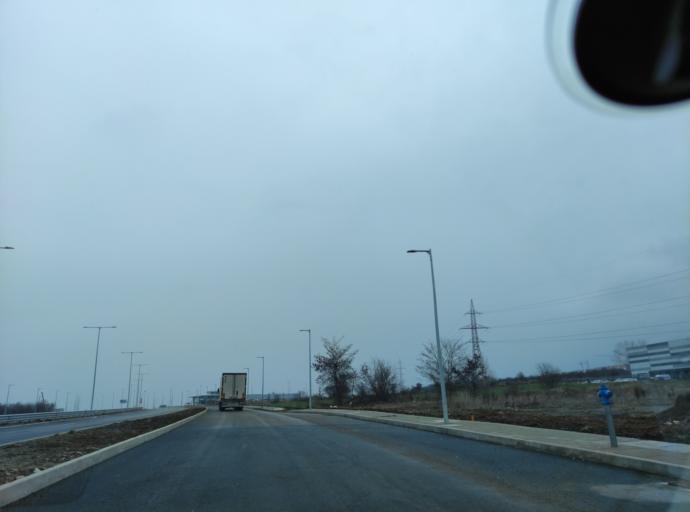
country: BG
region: Sofia-Capital
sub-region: Stolichna Obshtina
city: Sofia
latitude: 42.6212
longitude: 23.4353
